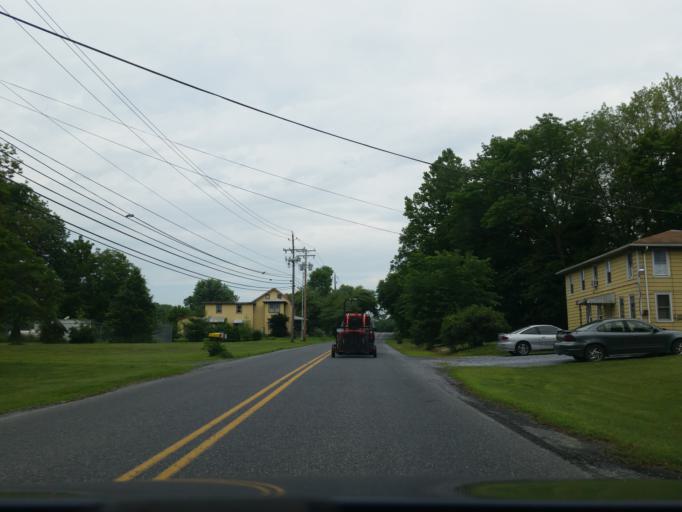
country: US
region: Pennsylvania
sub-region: Lebanon County
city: Jonestown
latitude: 40.4034
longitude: -76.5577
